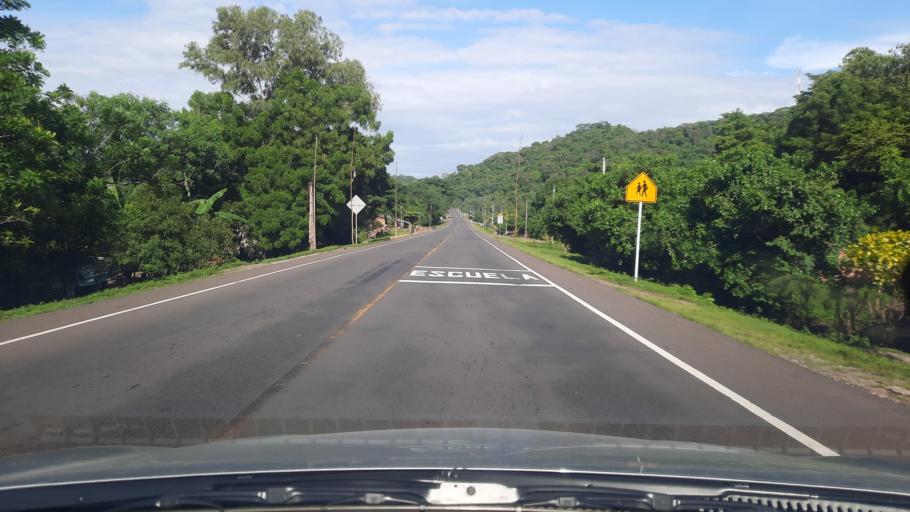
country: NI
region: Leon
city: Telica
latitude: 12.6982
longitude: -86.8681
